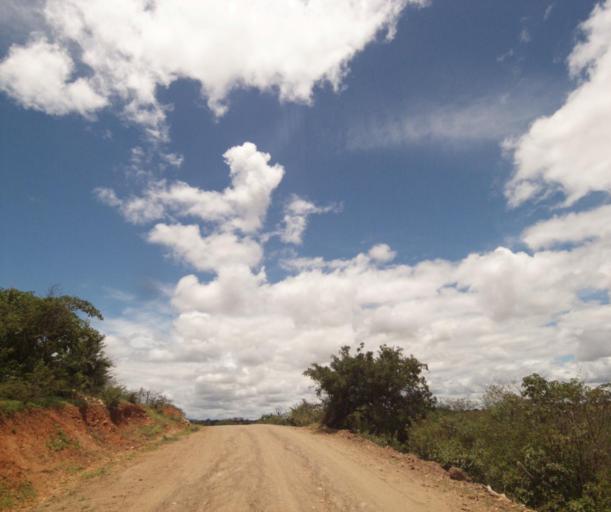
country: BR
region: Bahia
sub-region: Tanhacu
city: Tanhacu
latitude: -14.1650
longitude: -41.1674
